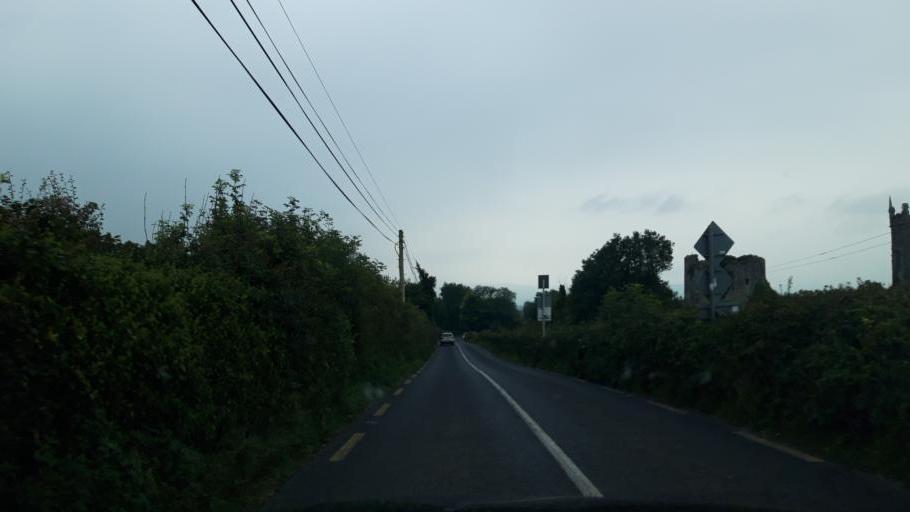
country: IE
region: Munster
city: Fethard
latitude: 52.4171
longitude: -7.7027
